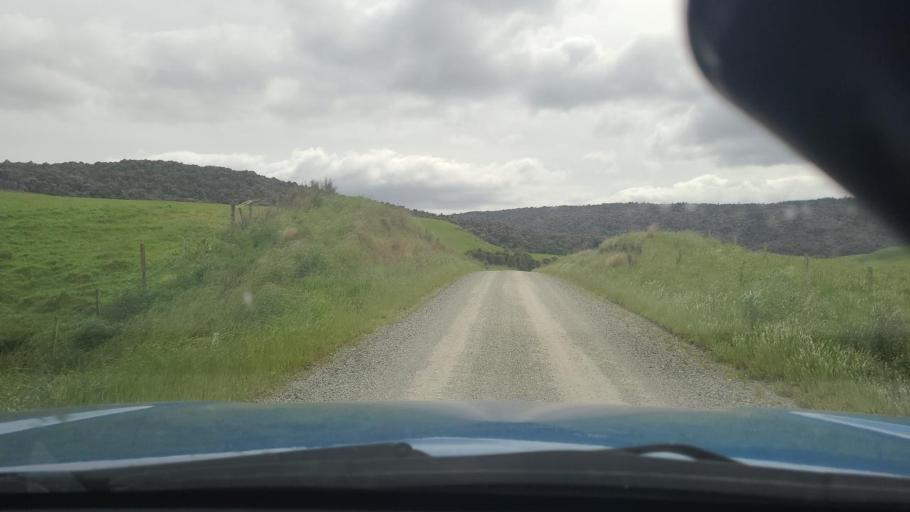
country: NZ
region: Otago
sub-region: Clutha District
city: Papatowai
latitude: -46.5091
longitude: 169.1490
